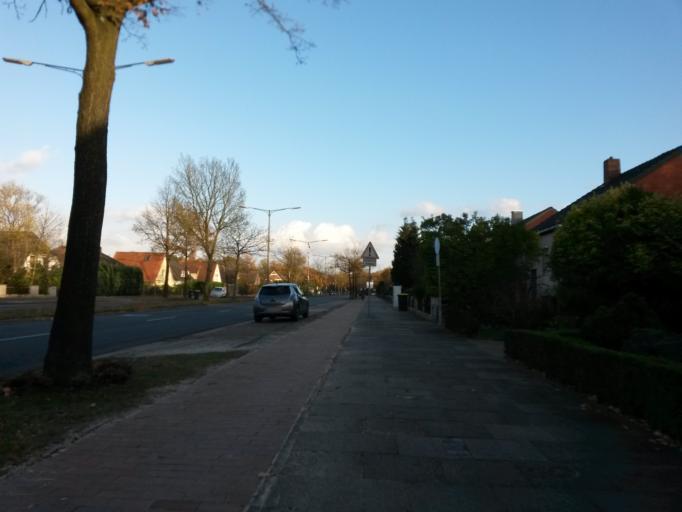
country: DE
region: Lower Saxony
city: Lilienthal
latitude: 53.0712
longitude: 8.9115
